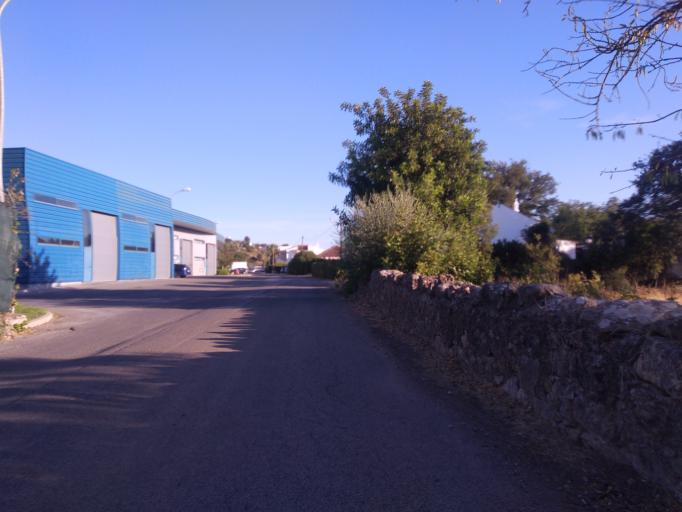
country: PT
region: Faro
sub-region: Sao Bras de Alportel
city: Sao Bras de Alportel
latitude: 37.1689
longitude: -7.8935
